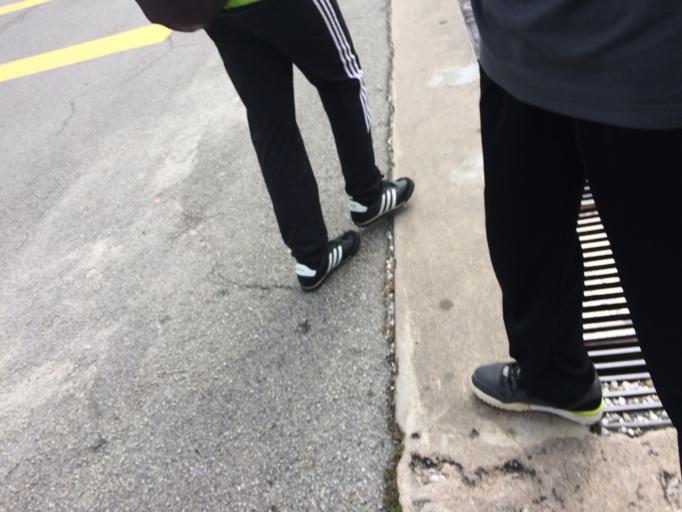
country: MY
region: Perak
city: Ipoh
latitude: 4.6055
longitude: 101.0935
